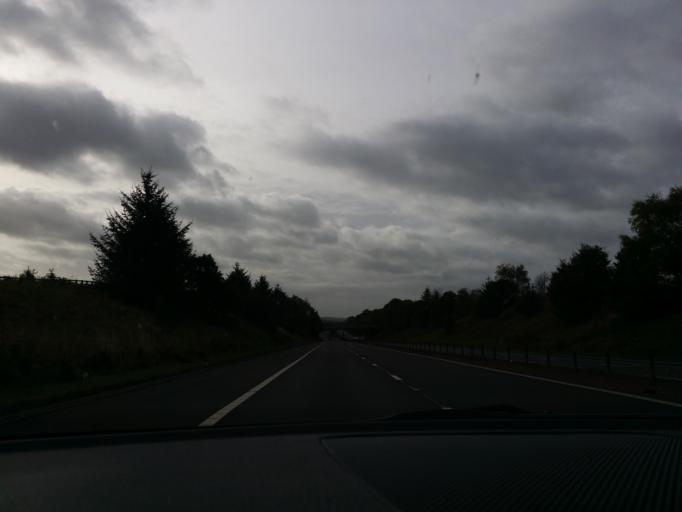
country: GB
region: Scotland
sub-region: West Lothian
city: Linlithgow
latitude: 55.9871
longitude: -3.5849
